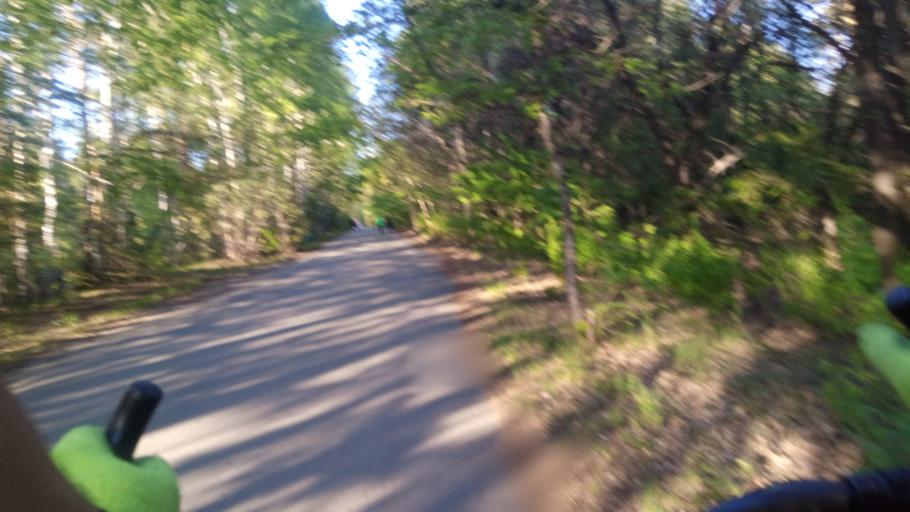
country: RU
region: Chelyabinsk
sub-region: Gorod Chelyabinsk
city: Chelyabinsk
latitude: 55.1530
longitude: 61.3425
